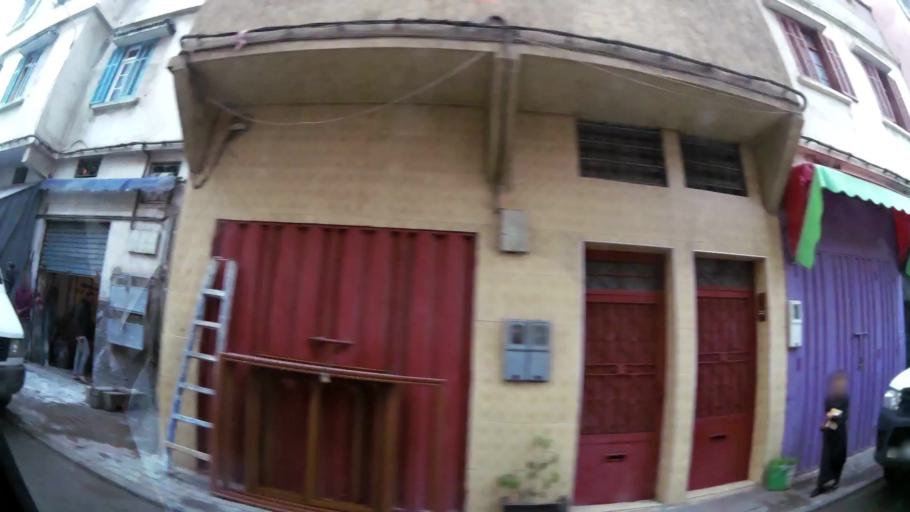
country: MA
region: Grand Casablanca
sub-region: Casablanca
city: Casablanca
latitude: 33.5539
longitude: -7.5776
